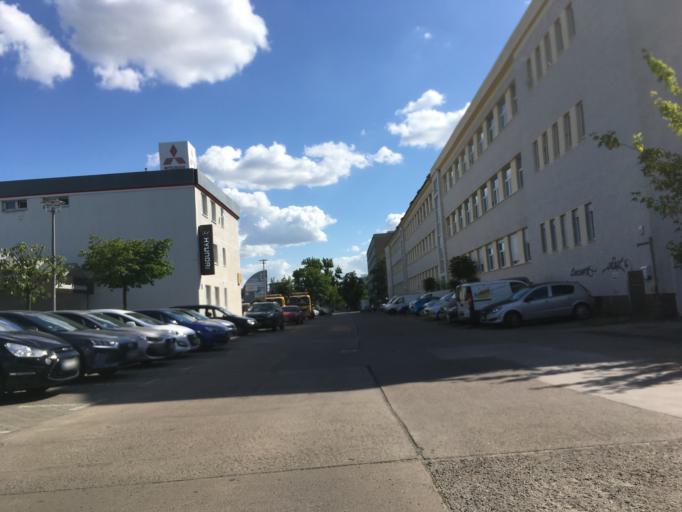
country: DE
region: Berlin
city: Alt-Hohenschoenhausen
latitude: 52.5435
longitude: 13.5005
